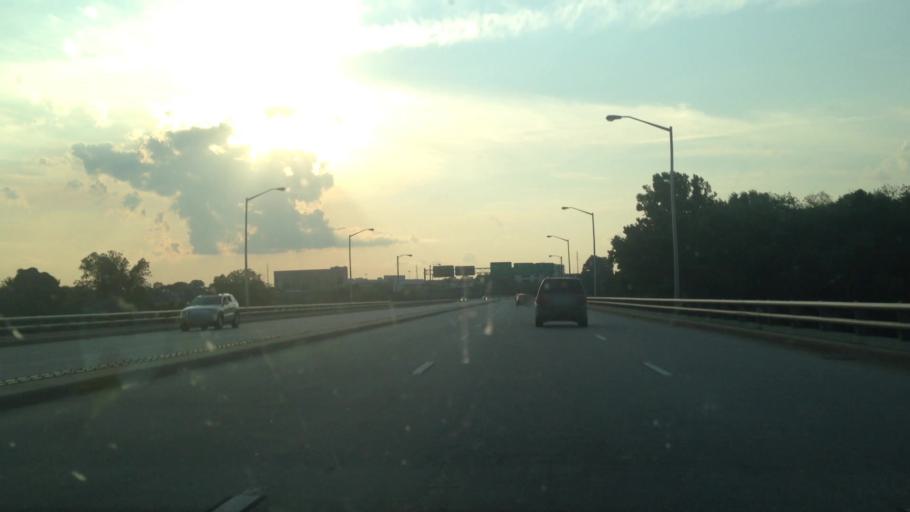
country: US
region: Virginia
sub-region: City of Danville
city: Danville
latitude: 36.5895
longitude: -79.4122
